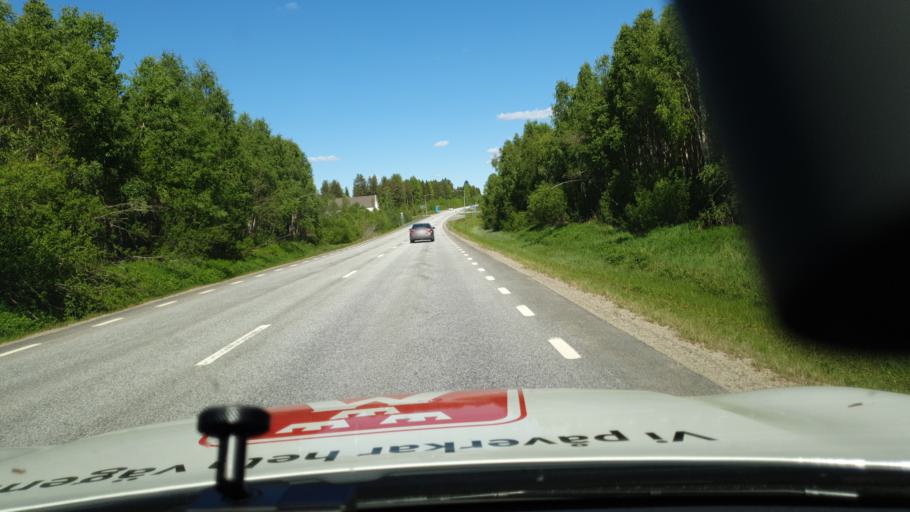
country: SE
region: Vaesterbotten
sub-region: Vannas Kommun
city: Vaennaes
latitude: 63.9953
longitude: 19.7287
